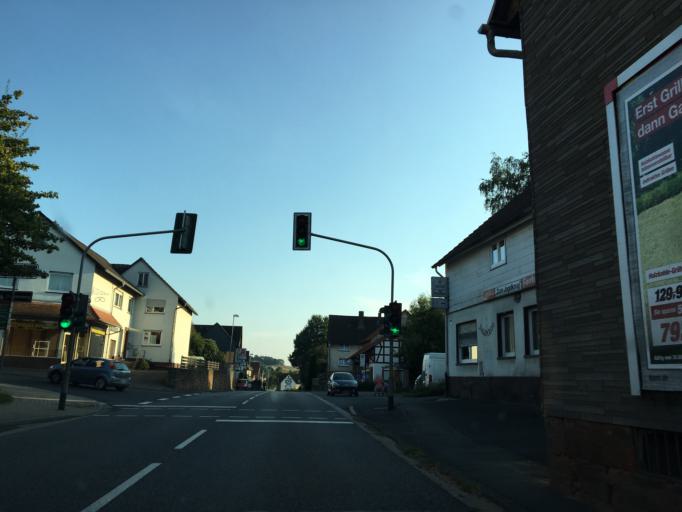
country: DE
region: Hesse
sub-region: Regierungsbezirk Giessen
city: Munchhausen
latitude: 50.9580
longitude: 8.7153
